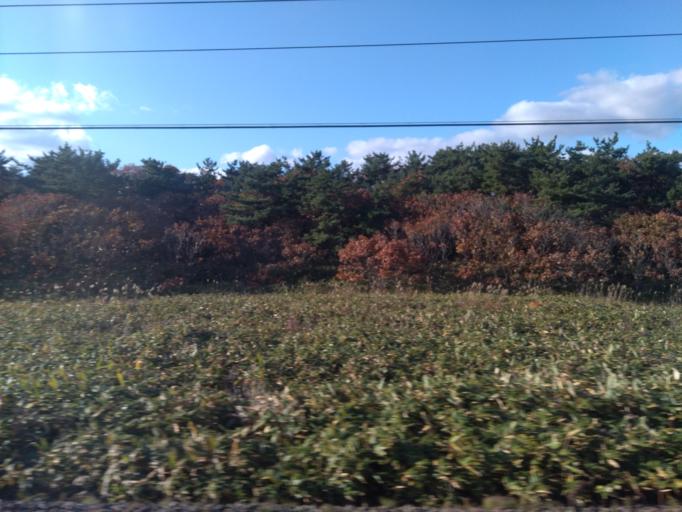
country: JP
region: Hokkaido
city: Niseko Town
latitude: 42.5560
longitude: 140.4243
